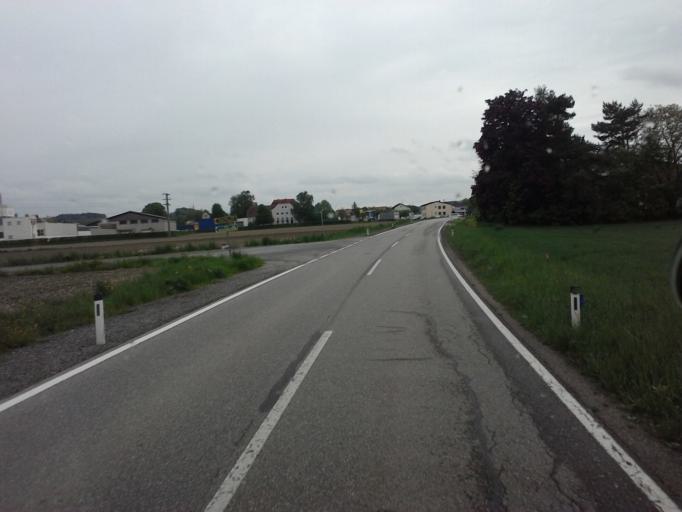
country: AT
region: Upper Austria
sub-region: Politischer Bezirk Scharding
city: Sankt Marienkirchen bei Schaerding
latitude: 48.3200
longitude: 13.4251
